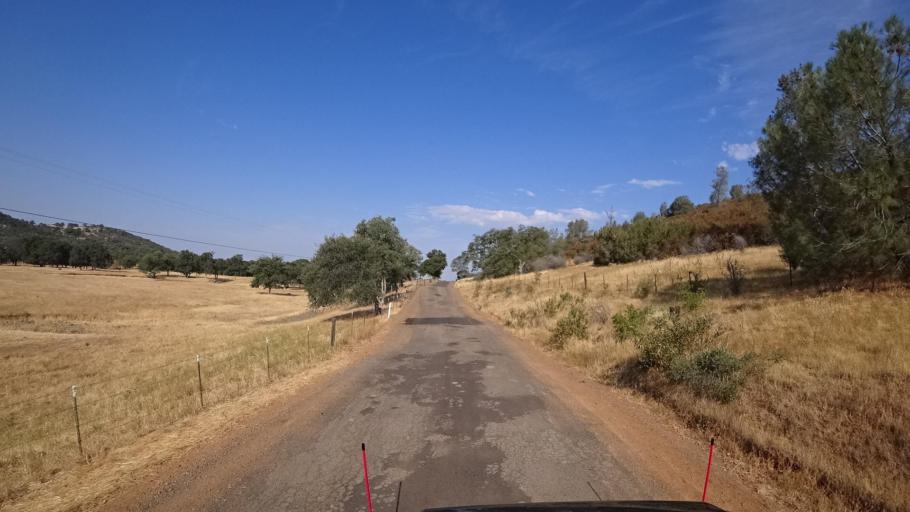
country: US
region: California
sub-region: Tuolumne County
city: Tuolumne City
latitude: 37.7212
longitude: -120.2780
